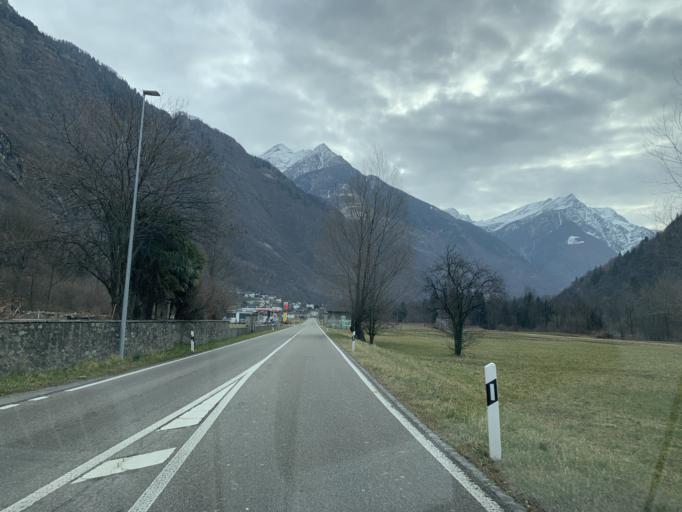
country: CH
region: Ticino
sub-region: Blenio District
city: Malvaglia
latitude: 46.4323
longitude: 8.9641
